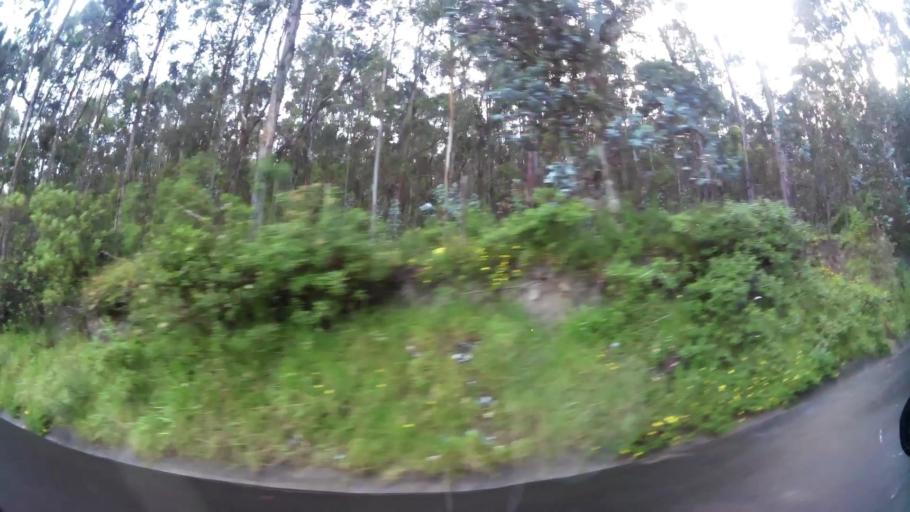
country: EC
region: Pichincha
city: Quito
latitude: -0.1080
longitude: -78.5223
